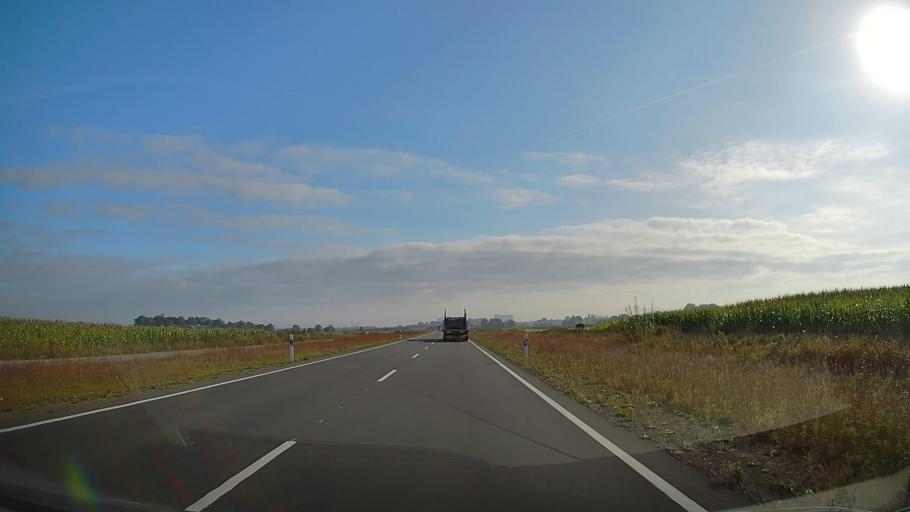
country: DE
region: Lower Saxony
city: Ovelgonne
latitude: 53.3251
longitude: 8.4318
